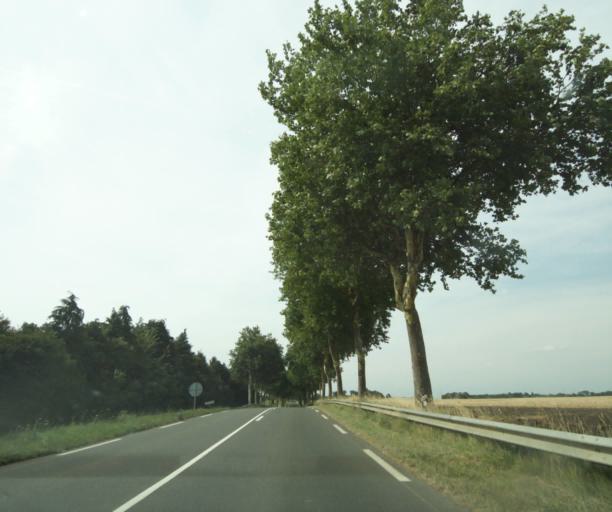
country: FR
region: Centre
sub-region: Departement d'Indre-et-Loire
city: Neuille-Pont-Pierre
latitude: 47.5658
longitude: 0.5489
